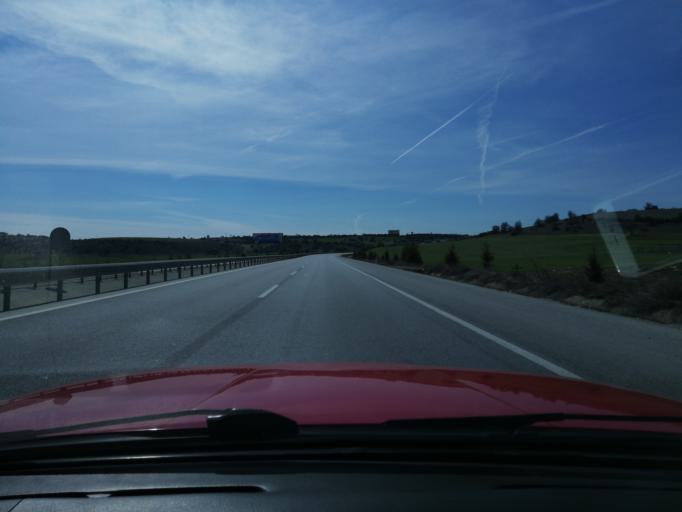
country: TR
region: Kuetahya
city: Sabuncu
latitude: 39.6627
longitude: 30.1560
